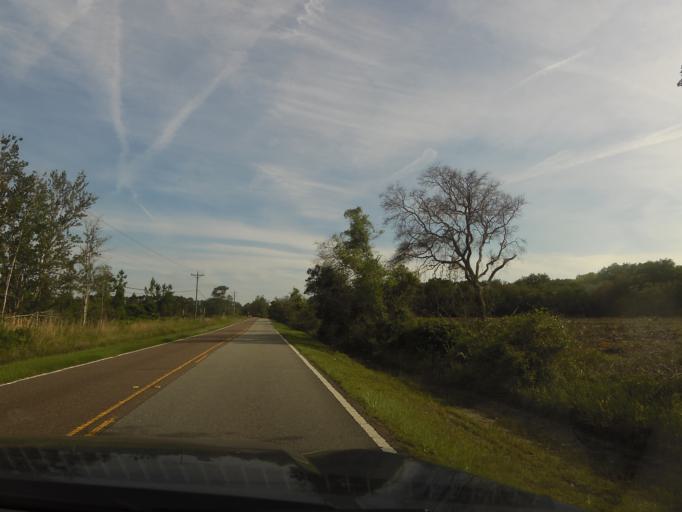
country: US
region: Florida
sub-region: Nassau County
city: Fernandina Beach
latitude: 30.4971
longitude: -81.4721
